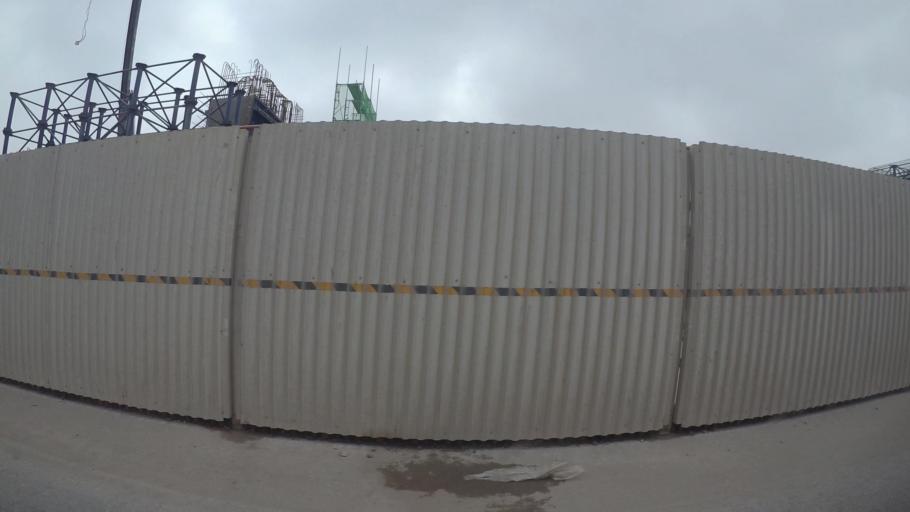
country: VN
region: Ha Noi
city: Tay Ho
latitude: 21.0654
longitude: 105.7846
